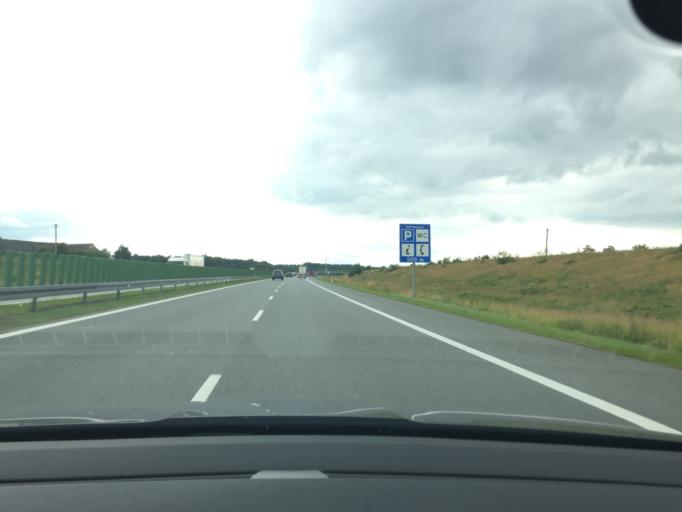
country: PL
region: Greater Poland Voivodeship
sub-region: Powiat nowotomyski
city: Lwowek
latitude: 52.3695
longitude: 16.2061
